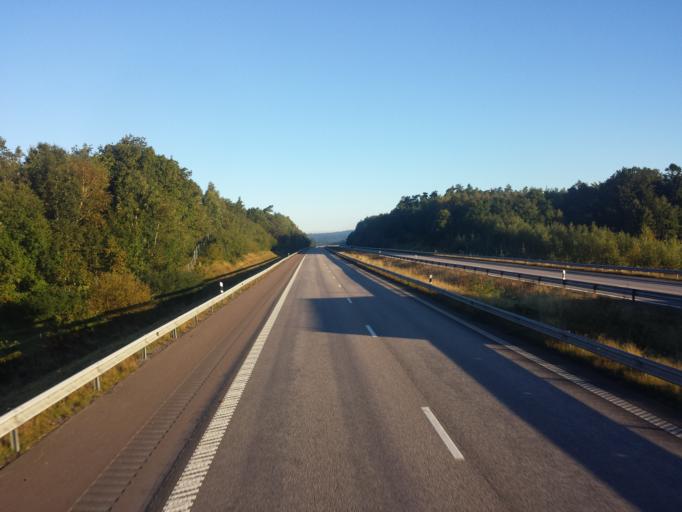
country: SE
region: Halland
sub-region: Varbergs Kommun
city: Veddige
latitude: 57.2093
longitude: 12.2420
